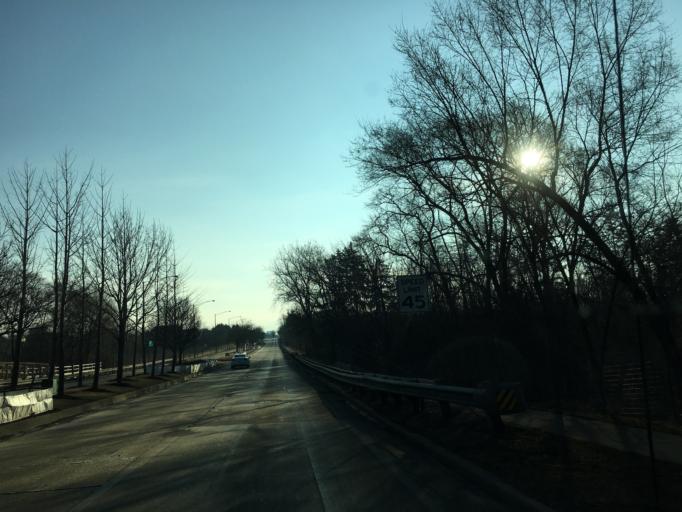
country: US
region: Illinois
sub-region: Cook County
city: Schaumburg
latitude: 42.0283
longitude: -88.0565
